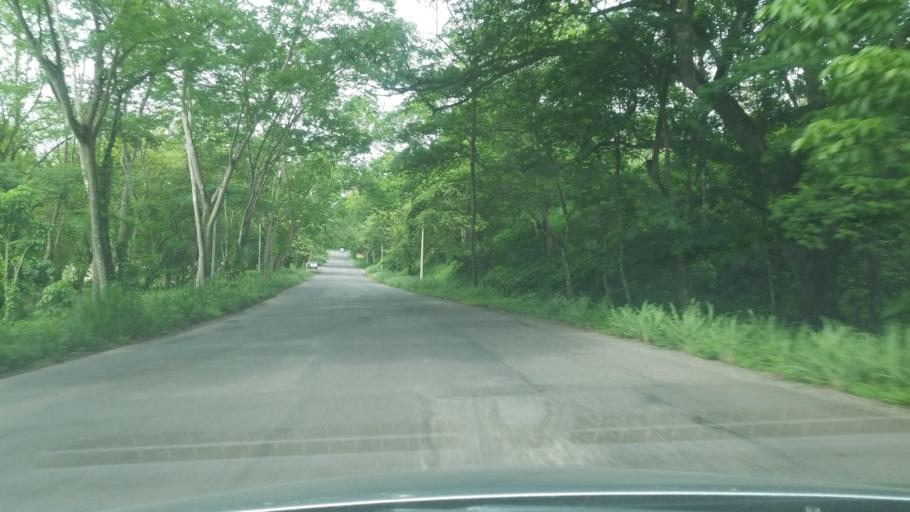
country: HN
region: Santa Barbara
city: Camalote
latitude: 15.3254
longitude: -88.3088
